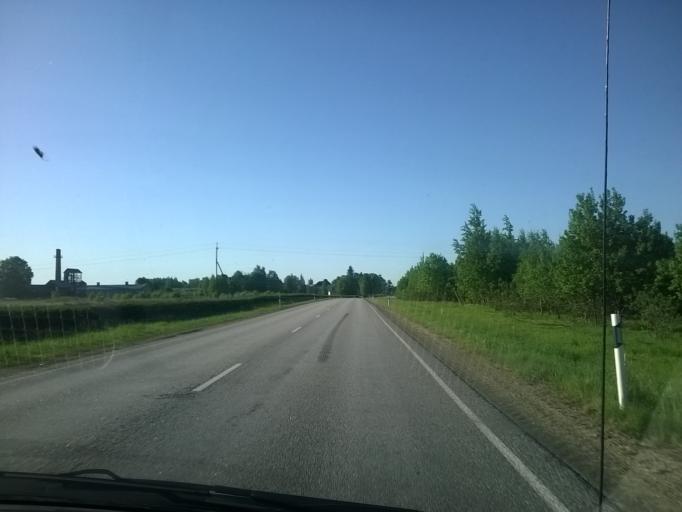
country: EE
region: Valgamaa
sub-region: Valga linn
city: Valga
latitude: 57.9308
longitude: 26.1733
